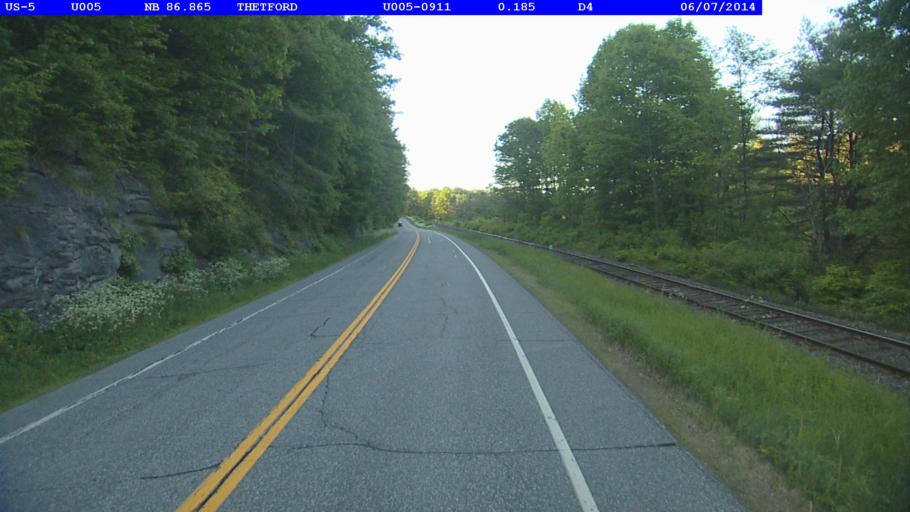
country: US
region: New Hampshire
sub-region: Grafton County
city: Lyme
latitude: 43.7744
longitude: -72.2060
